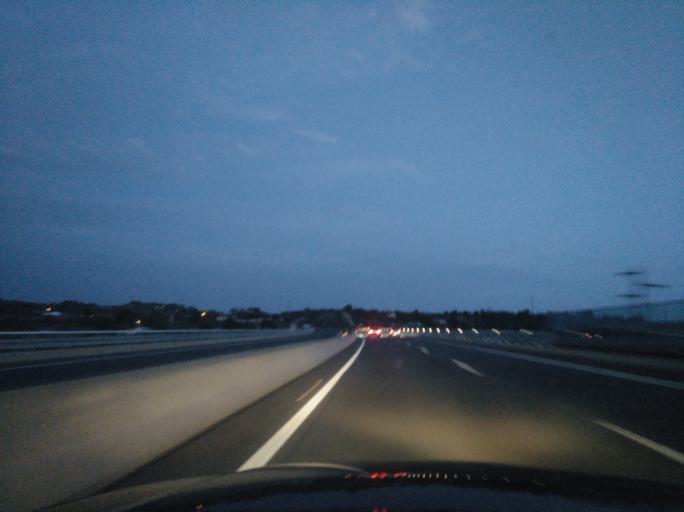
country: PT
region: Faro
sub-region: Lagoa
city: Lagoa
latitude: 37.1404
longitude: -8.4130
